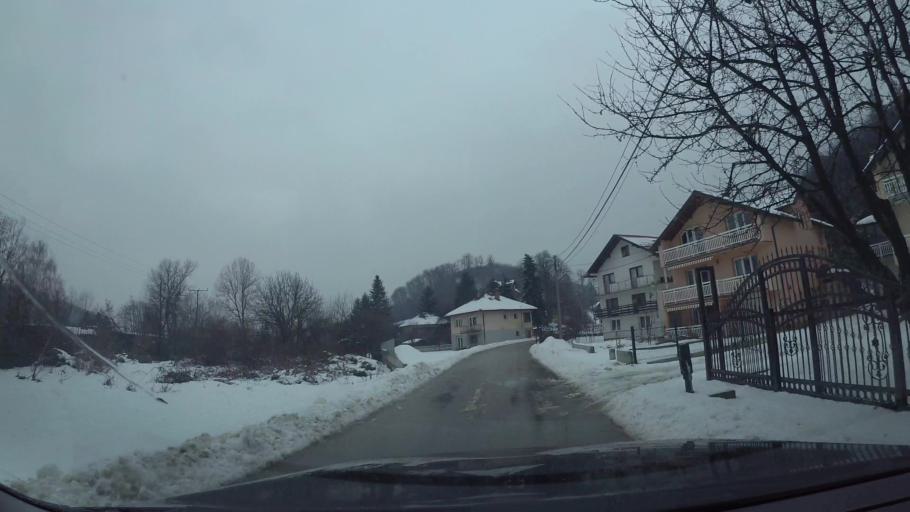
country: BA
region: Federation of Bosnia and Herzegovina
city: Hadzici
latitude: 43.8412
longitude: 18.2593
